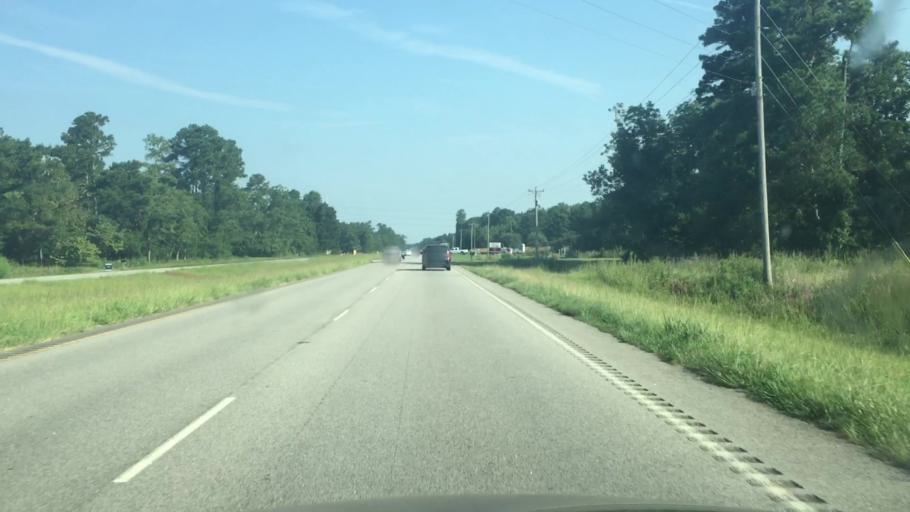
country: US
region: South Carolina
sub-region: Horry County
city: Little River
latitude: 33.9622
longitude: -78.7379
